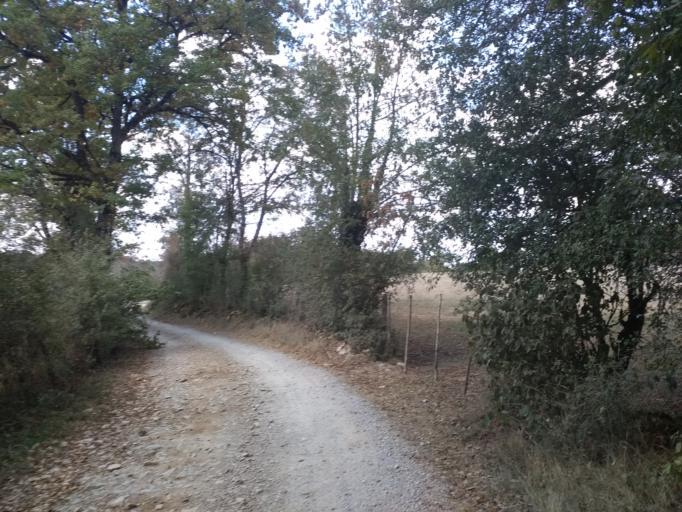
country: FR
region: Midi-Pyrenees
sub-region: Departement de l'Aveyron
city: Bozouls
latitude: 44.4599
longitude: 2.6768
